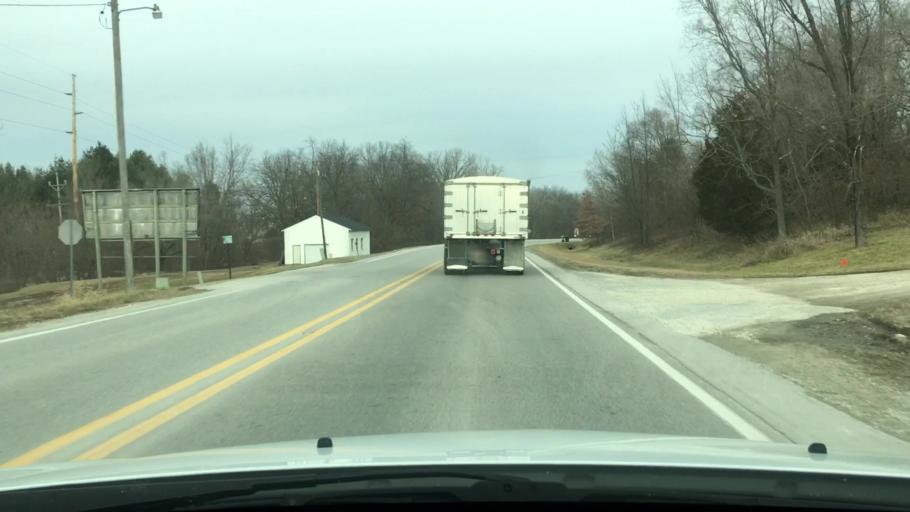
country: US
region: Illinois
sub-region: Pike County
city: Pittsfield
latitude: 39.6216
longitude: -90.8005
